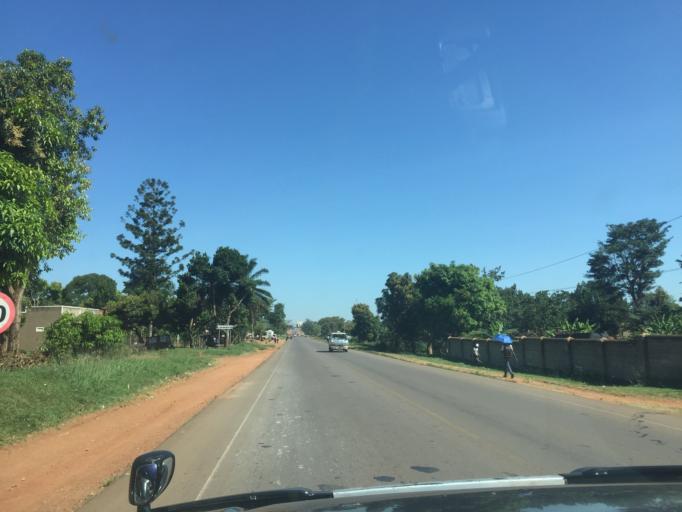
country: UG
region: Central Region
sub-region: Luwero District
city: Luwero
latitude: 0.8189
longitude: 32.5035
